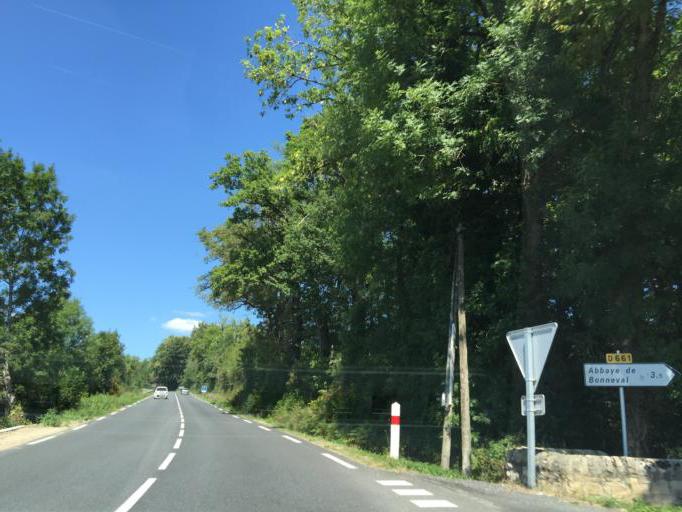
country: FR
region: Midi-Pyrenees
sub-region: Departement de l'Aveyron
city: Espalion
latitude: 44.5447
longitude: 2.7782
